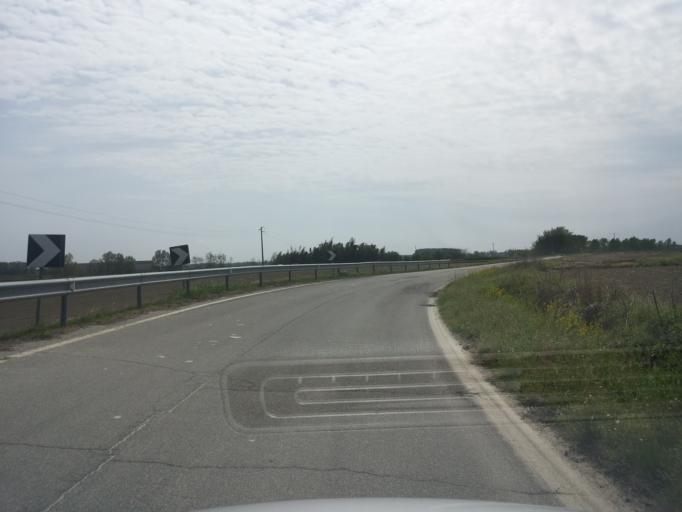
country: IT
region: Piedmont
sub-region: Provincia di Vercelli
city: Motta De Conti
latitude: 45.2078
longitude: 8.5137
